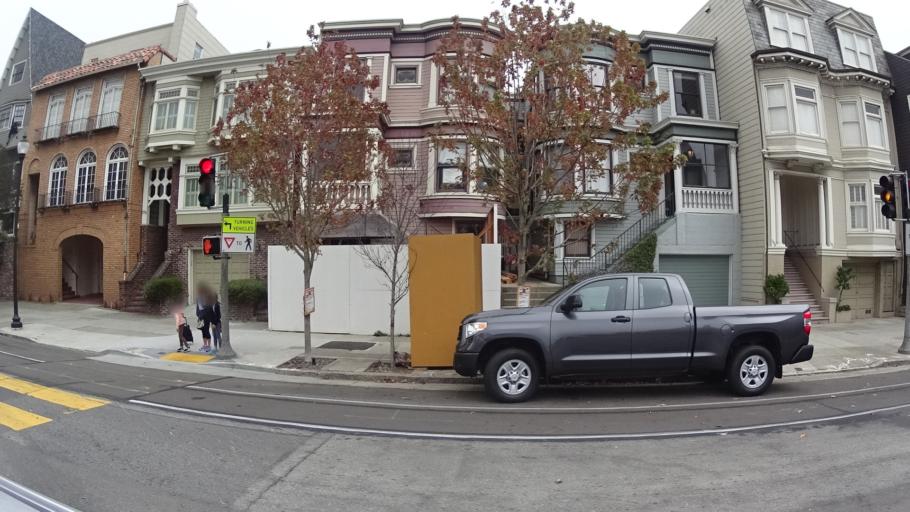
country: US
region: California
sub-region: San Francisco County
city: San Francisco
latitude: 37.7870
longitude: -122.4593
